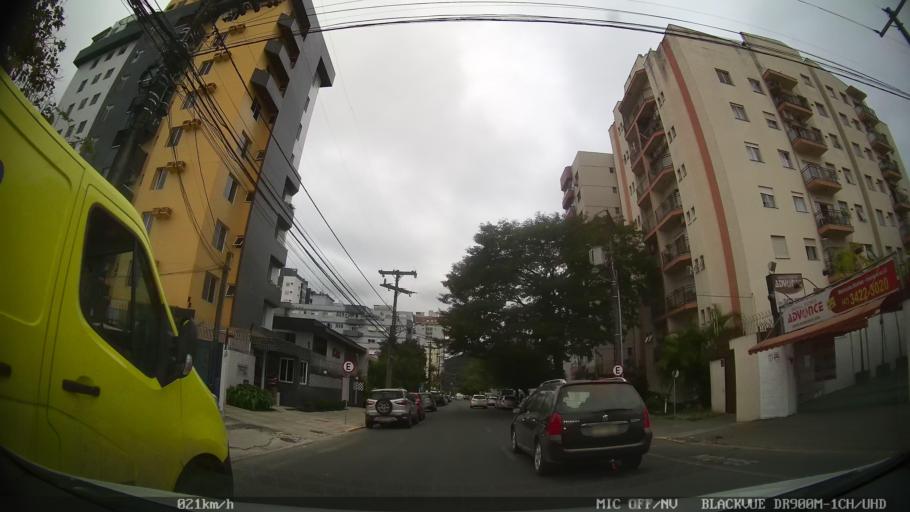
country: BR
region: Santa Catarina
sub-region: Joinville
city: Joinville
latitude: -26.2961
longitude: -48.8473
